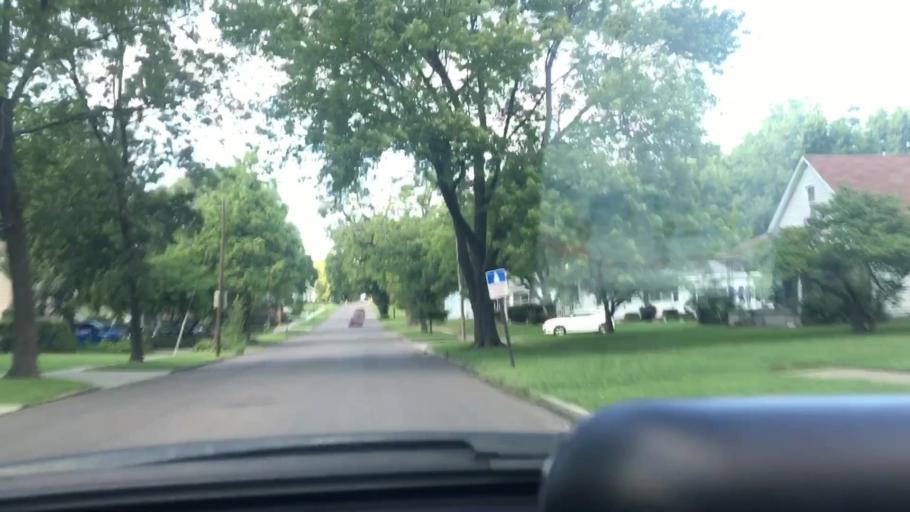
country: US
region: Missouri
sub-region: Pettis County
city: Sedalia
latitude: 38.7006
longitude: -93.2366
